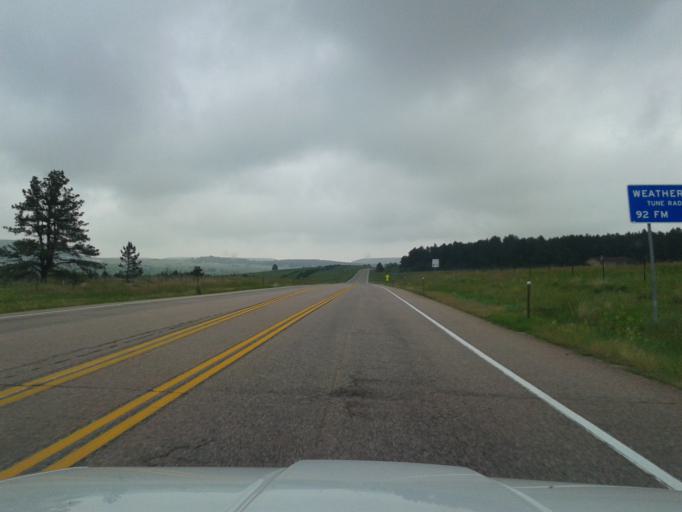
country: US
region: Colorado
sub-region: El Paso County
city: Woodmoor
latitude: 39.1320
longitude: -104.7665
